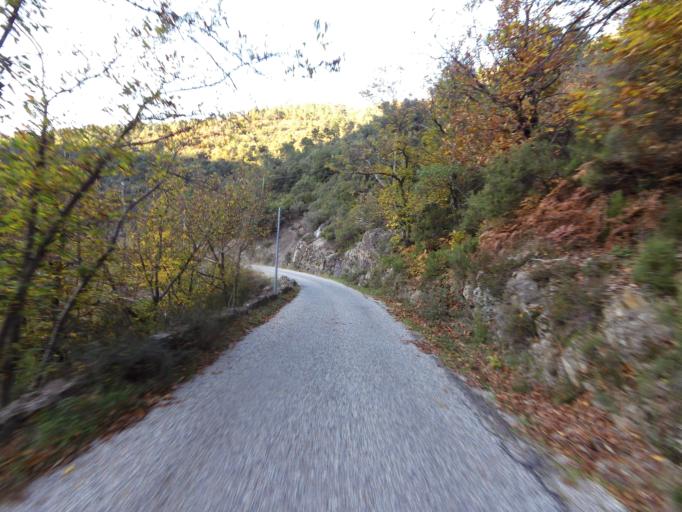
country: FR
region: Rhone-Alpes
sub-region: Departement de l'Ardeche
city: Lablachere
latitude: 44.5244
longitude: 4.1399
